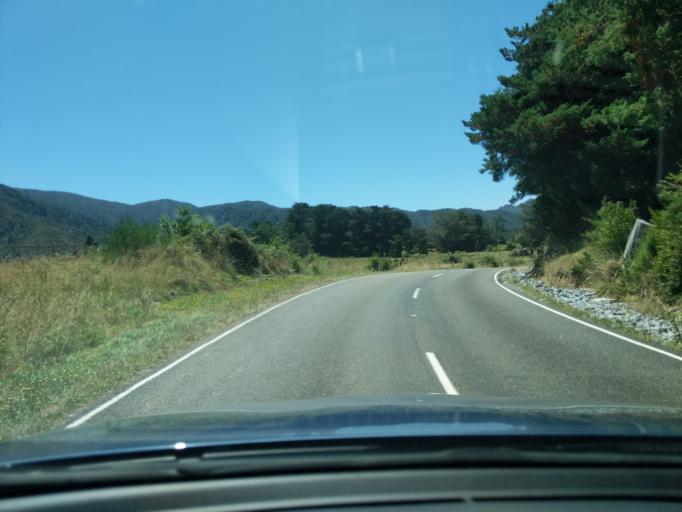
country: NZ
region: Tasman
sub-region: Tasman District
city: Takaka
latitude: -40.7561
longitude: 172.5613
